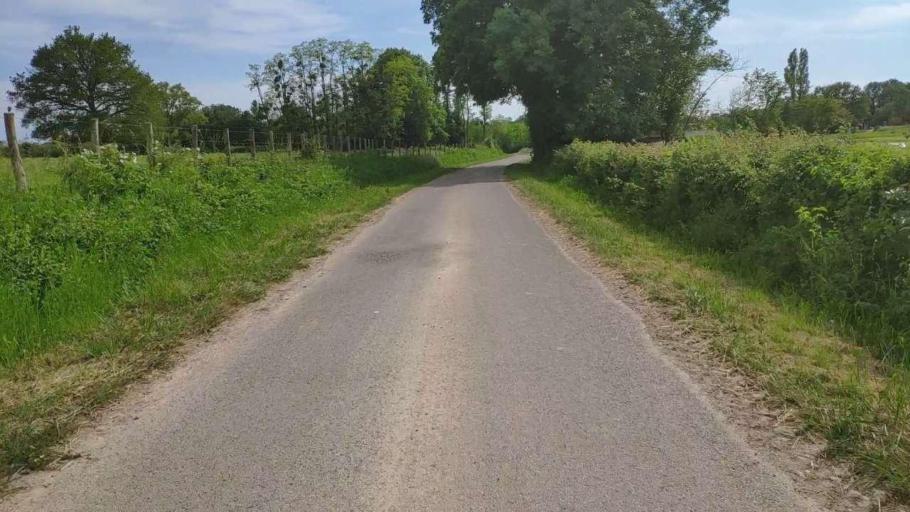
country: FR
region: Franche-Comte
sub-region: Departement du Jura
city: Bletterans
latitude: 46.8134
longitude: 5.3540
